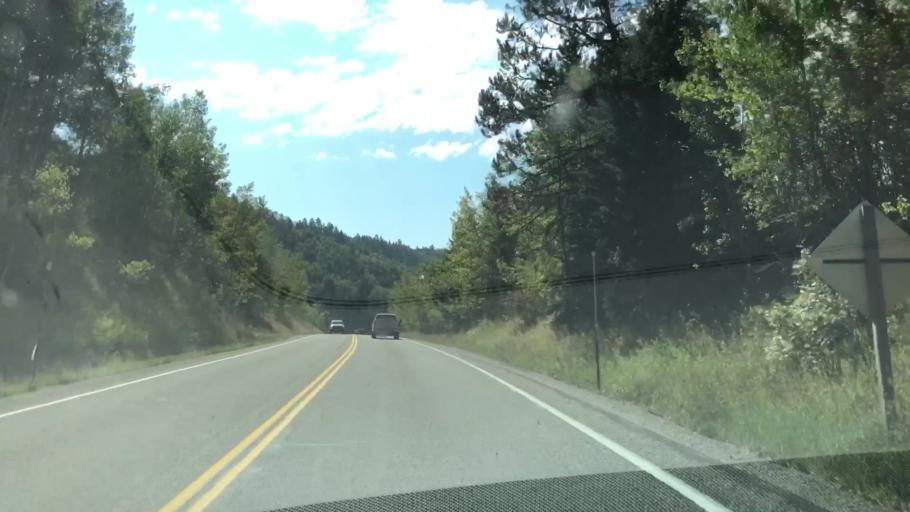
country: US
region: Idaho
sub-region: Teton County
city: Victor
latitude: 43.2804
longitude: -111.1178
